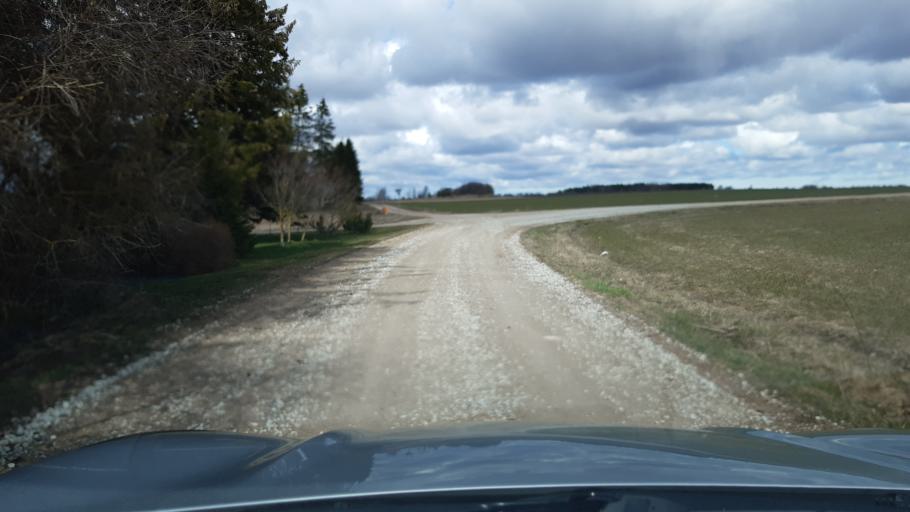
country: EE
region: Harju
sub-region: Rae vald
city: Vaida
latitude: 59.0710
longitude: 25.0943
